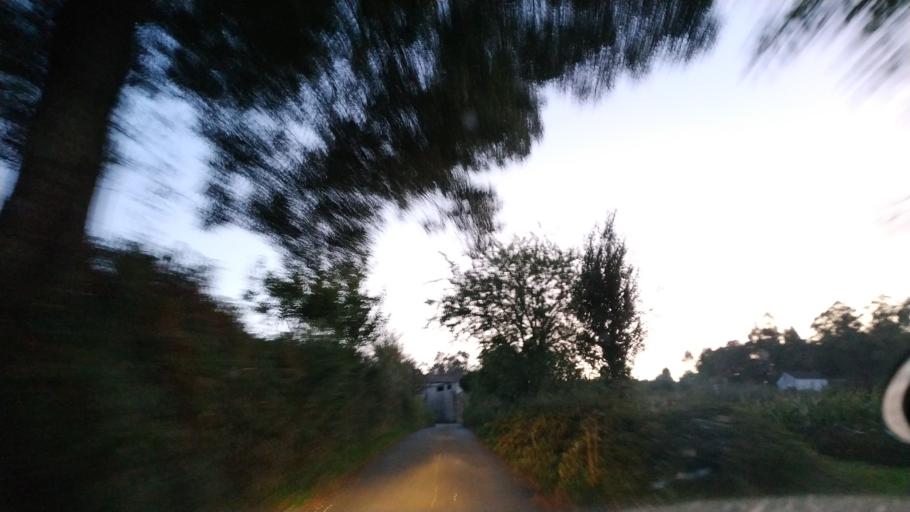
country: ES
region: Galicia
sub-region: Provincia da Coruna
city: Negreira
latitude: 42.9134
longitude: -8.7641
